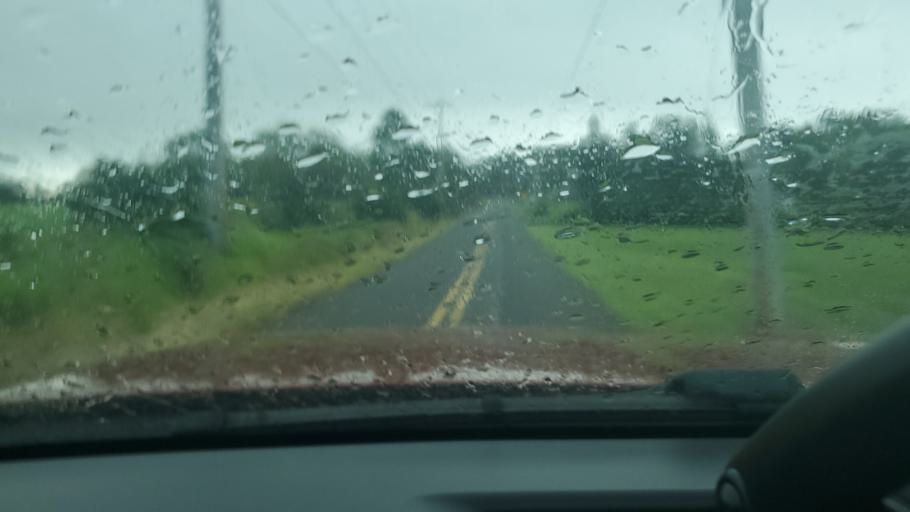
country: US
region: Pennsylvania
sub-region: Montgomery County
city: Woxall
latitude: 40.3085
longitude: -75.5131
